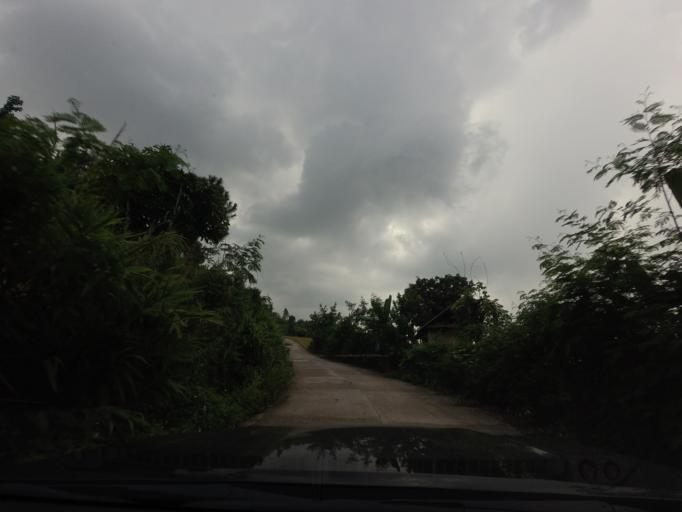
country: TH
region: Nan
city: Bo Kluea
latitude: 19.3512
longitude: 101.1708
